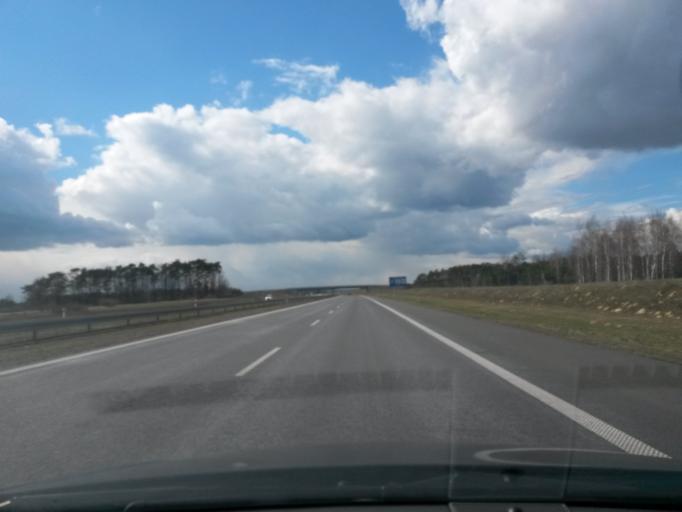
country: PL
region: Greater Poland Voivodeship
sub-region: Powiat turecki
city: Wladyslawow
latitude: 52.1494
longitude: 18.4949
